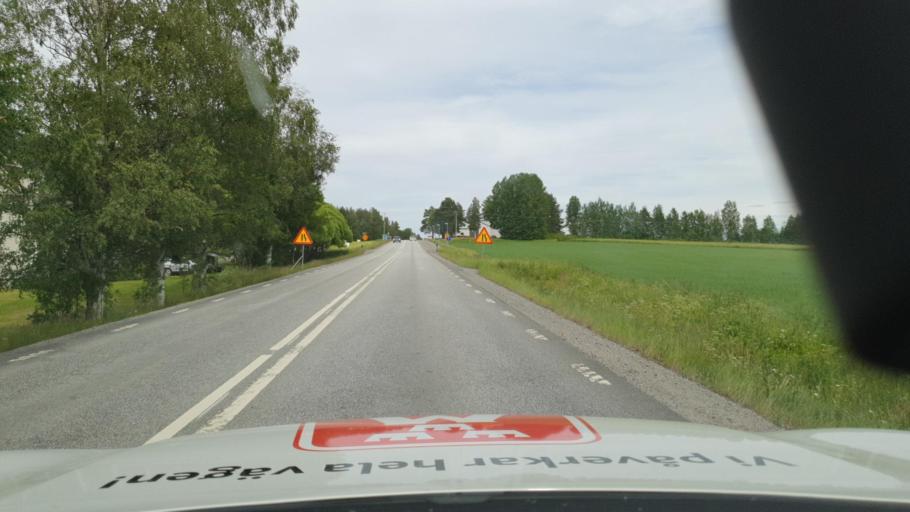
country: SE
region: Vaesterbotten
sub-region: Skelleftea Kommun
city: Burtraesk
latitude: 64.4913
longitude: 20.7087
